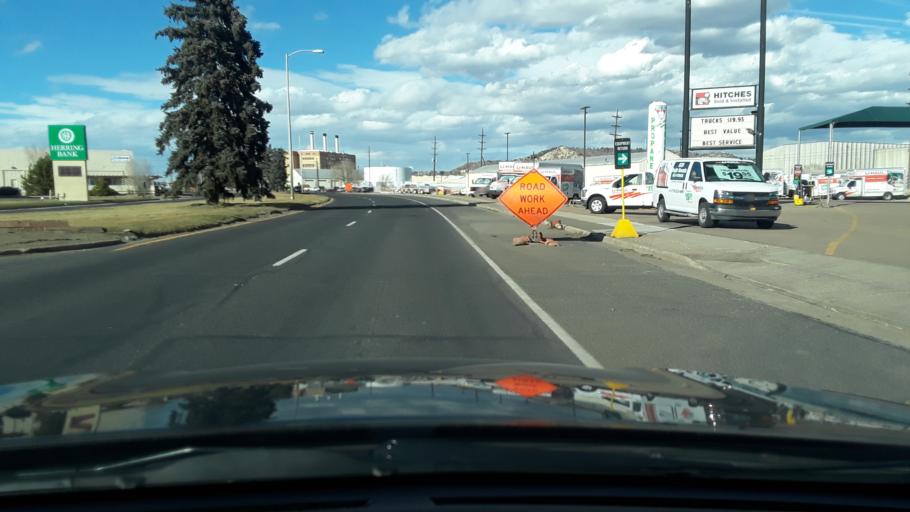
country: US
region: Colorado
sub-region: El Paso County
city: Colorado Springs
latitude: 38.8763
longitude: -104.8190
